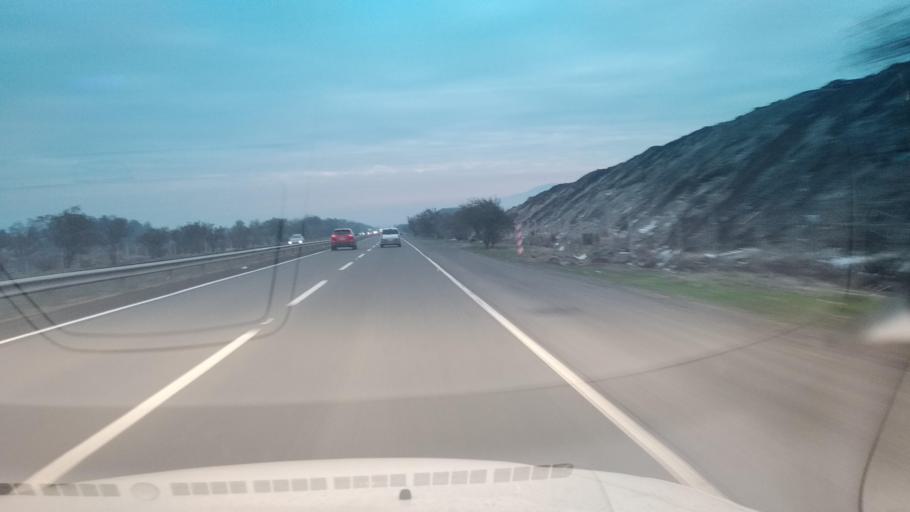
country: CL
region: Santiago Metropolitan
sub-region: Provincia de Chacabuco
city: Chicureo Abajo
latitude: -33.1970
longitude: -70.6588
